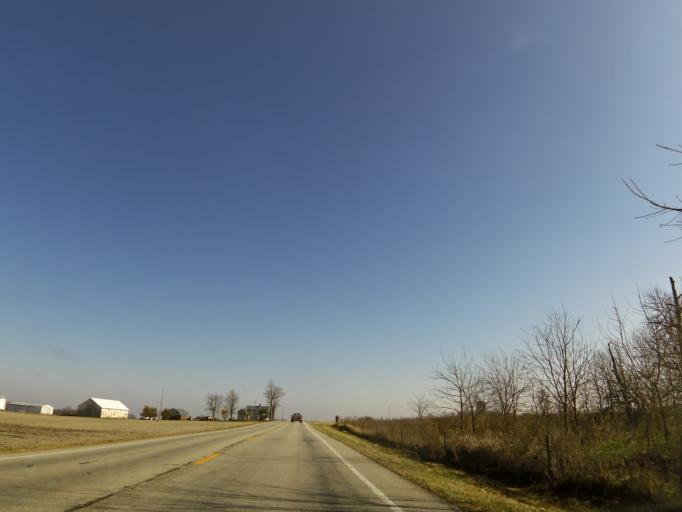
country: US
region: Indiana
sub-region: Fayette County
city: Connersville
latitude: 39.6274
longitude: -85.2701
